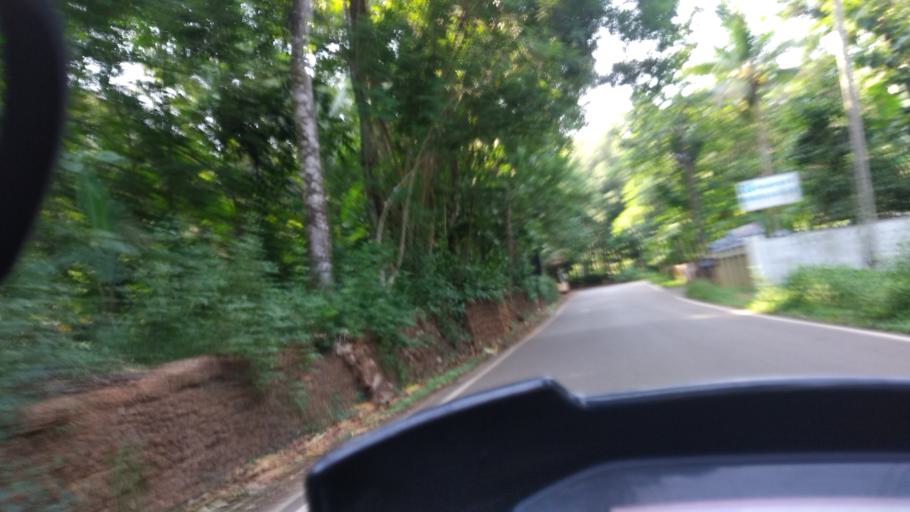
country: IN
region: Kerala
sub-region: Ernakulam
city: Piravam
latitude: 9.8555
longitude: 76.5250
